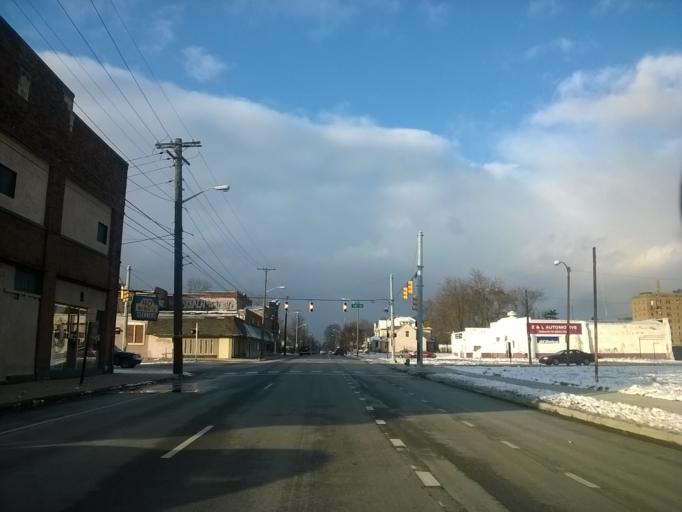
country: US
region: Indiana
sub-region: Marion County
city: Indianapolis
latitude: 39.8170
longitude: -86.1591
